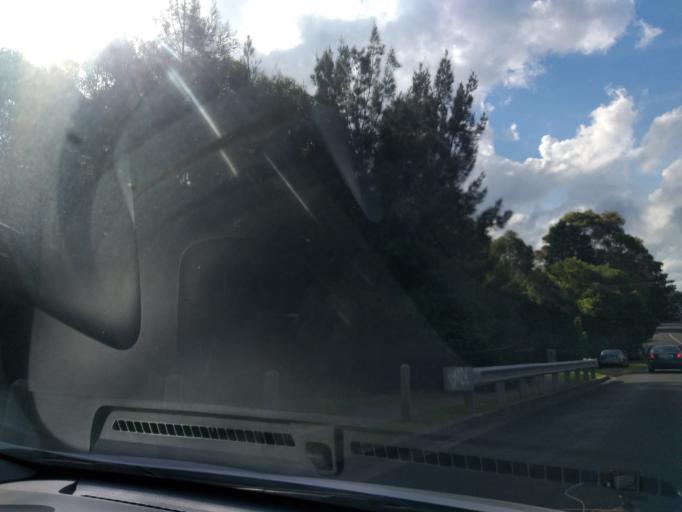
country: AU
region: New South Wales
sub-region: Wollongong
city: Helensburgh
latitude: -34.1955
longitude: 150.9812
